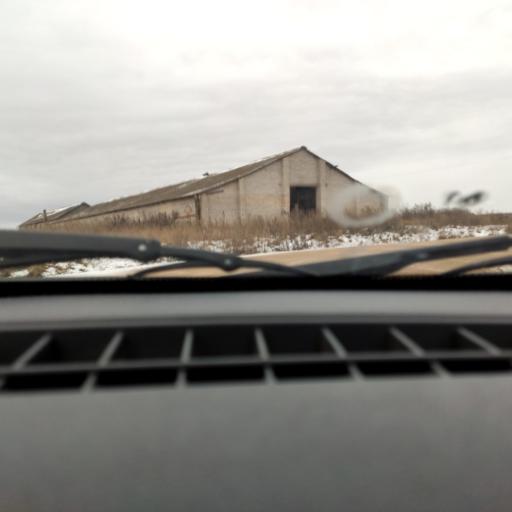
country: RU
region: Bashkortostan
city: Tolbazy
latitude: 54.2574
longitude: 55.9267
